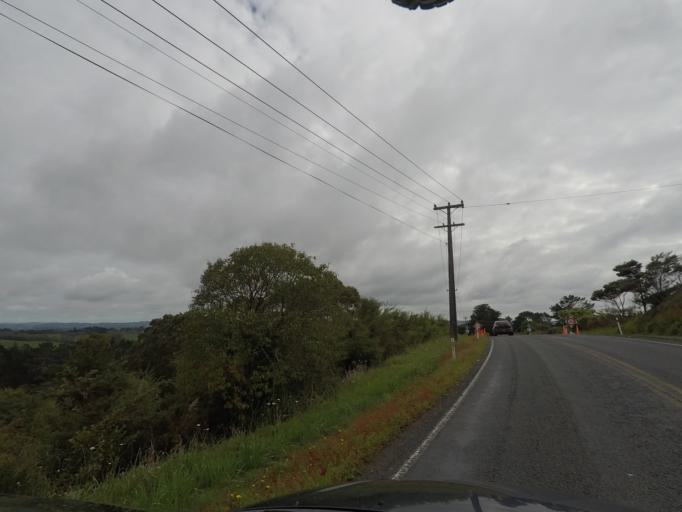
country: NZ
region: Auckland
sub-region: Auckland
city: Rosebank
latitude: -36.8377
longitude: 174.5848
